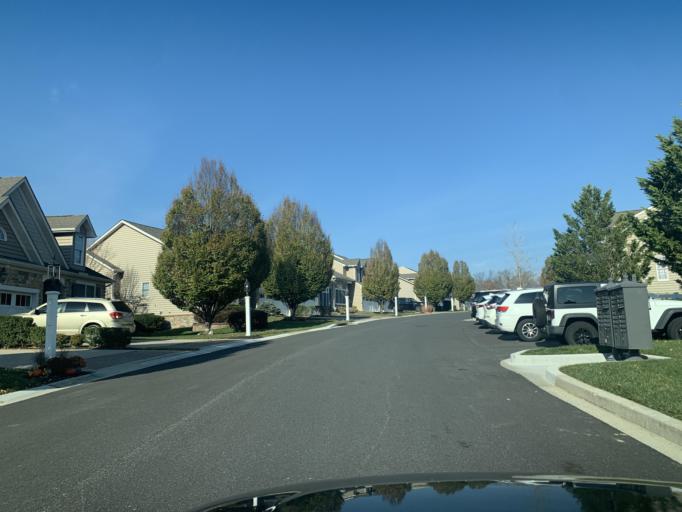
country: US
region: Maryland
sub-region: Harford County
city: Havre de Grace
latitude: 39.5453
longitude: -76.1203
